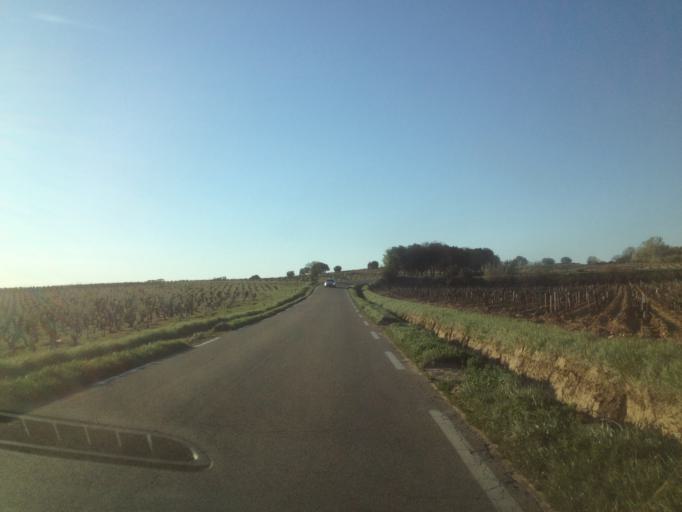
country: FR
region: Provence-Alpes-Cote d'Azur
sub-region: Departement du Vaucluse
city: Chateauneuf-du-Pape
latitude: 44.0883
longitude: 4.8296
